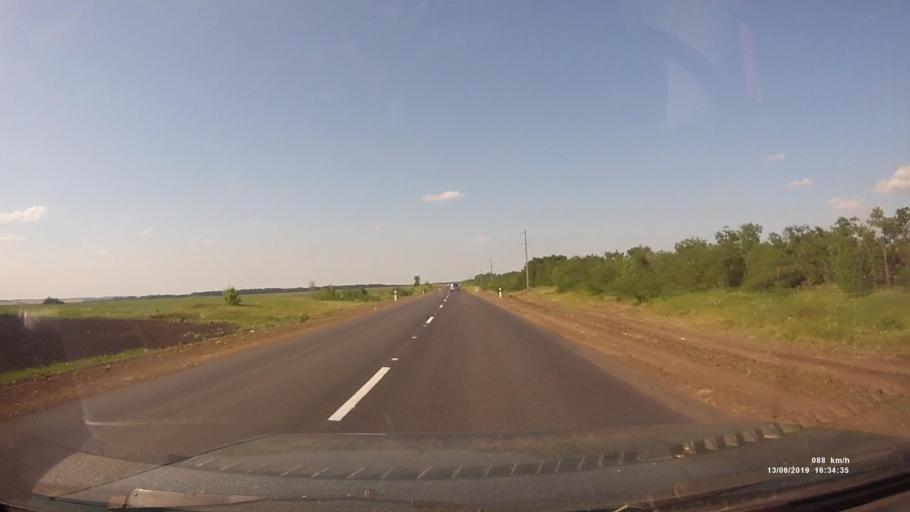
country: RU
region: Rostov
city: Kazanskaya
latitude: 49.8735
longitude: 41.2937
